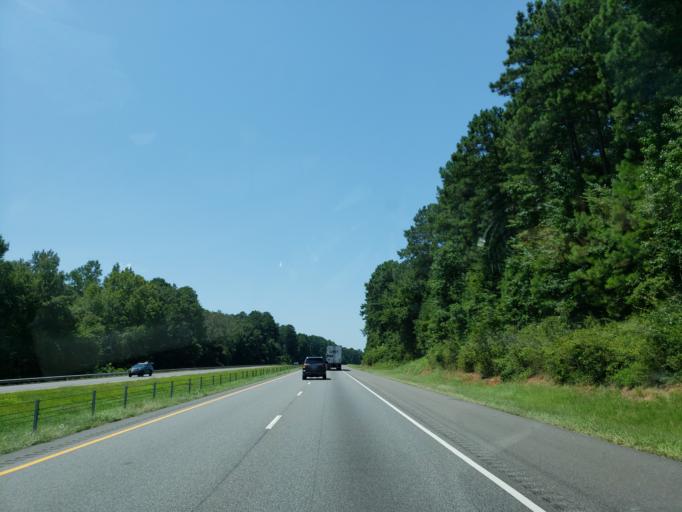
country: US
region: Alabama
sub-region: Greene County
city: Eutaw
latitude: 32.8805
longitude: -87.9096
